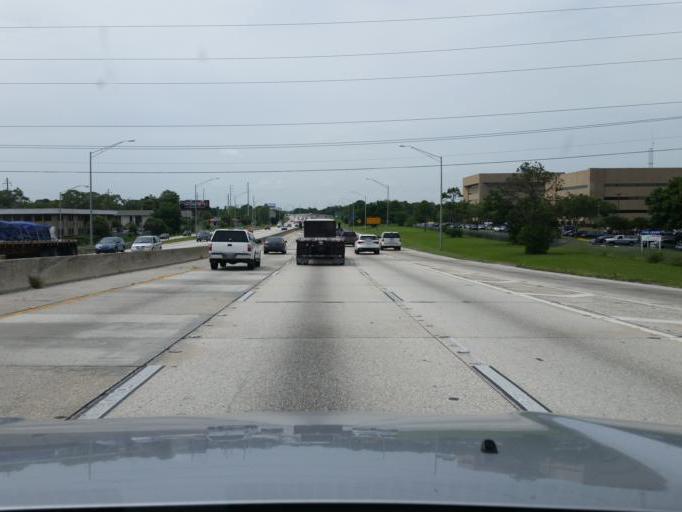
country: US
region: Florida
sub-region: Orange County
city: Eatonville
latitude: 28.6046
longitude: -81.3865
